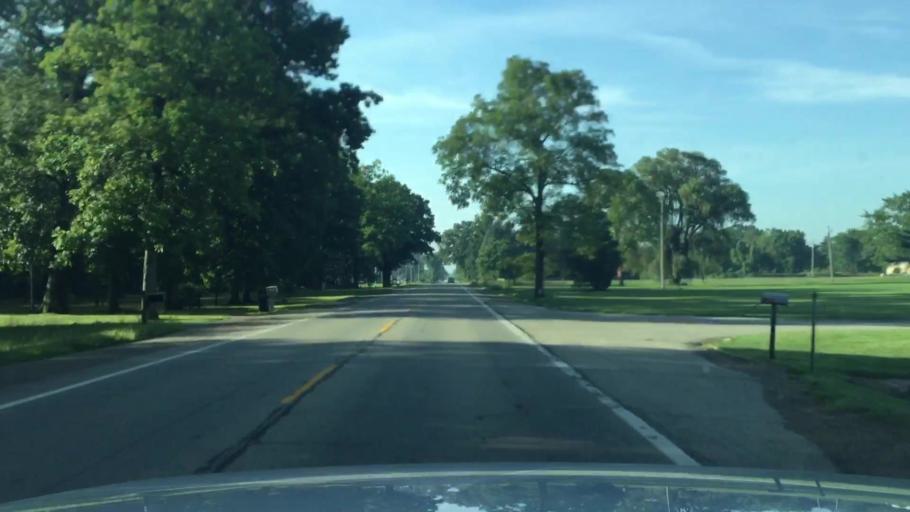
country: US
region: Michigan
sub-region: Lenawee County
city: Manitou Beach-Devils Lake
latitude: 42.0077
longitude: -84.3496
